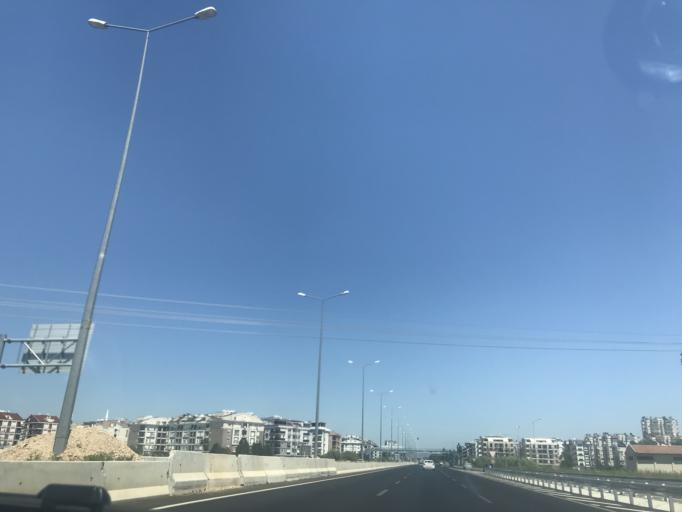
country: TR
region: Antalya
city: Cakirlar
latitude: 36.8493
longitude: 30.6022
